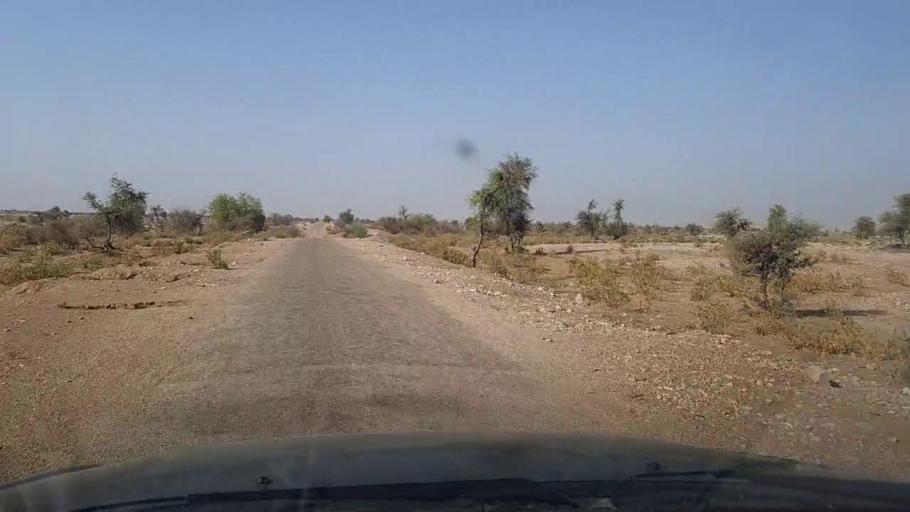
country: PK
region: Sindh
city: Sann
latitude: 25.9257
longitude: 68.0184
